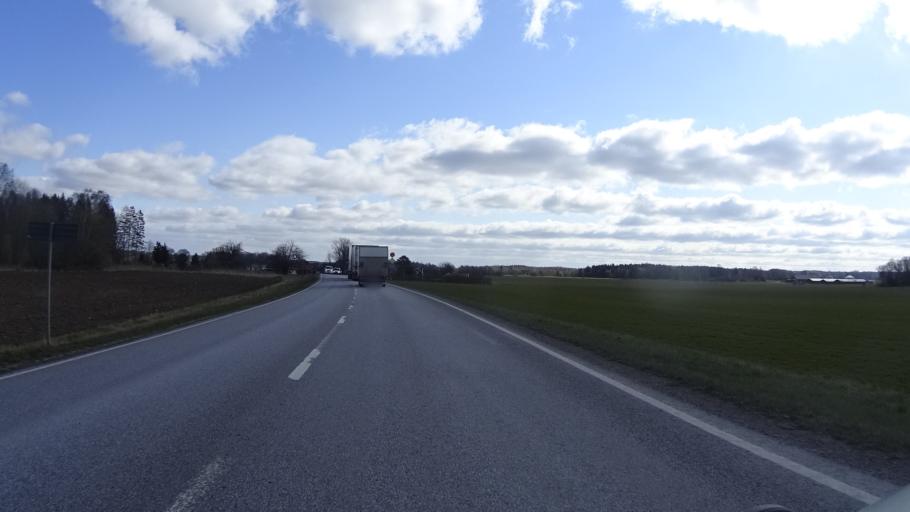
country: SE
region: OEstergoetland
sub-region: Mjolby Kommun
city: Mantorp
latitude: 58.3781
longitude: 15.2540
